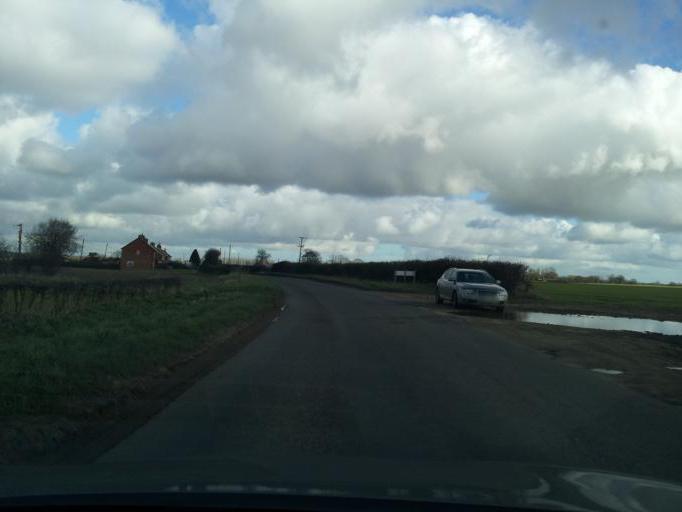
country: GB
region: England
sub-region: Norfolk
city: Mattishall
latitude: 52.6587
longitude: 1.0434
